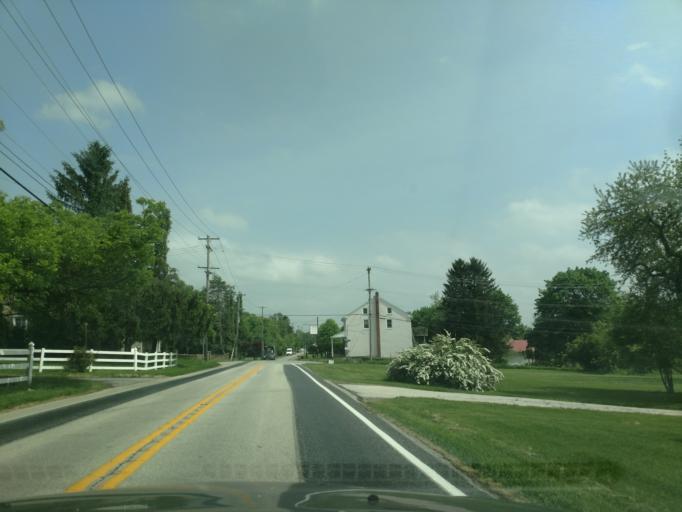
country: US
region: Pennsylvania
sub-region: Chester County
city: Spring City
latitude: 40.1693
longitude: -75.6060
